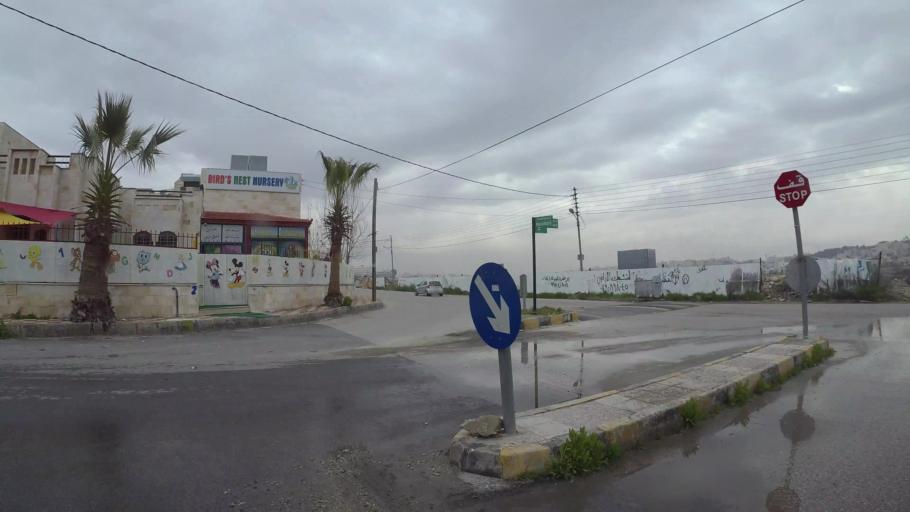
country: JO
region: Amman
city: Umm as Summaq
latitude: 31.8980
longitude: 35.8467
